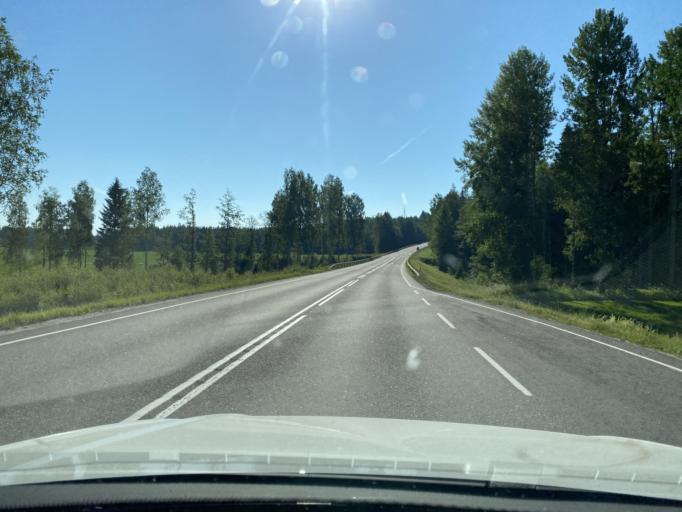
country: FI
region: Haeme
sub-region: Riihimaeki
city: Loppi
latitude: 60.7482
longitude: 24.3325
